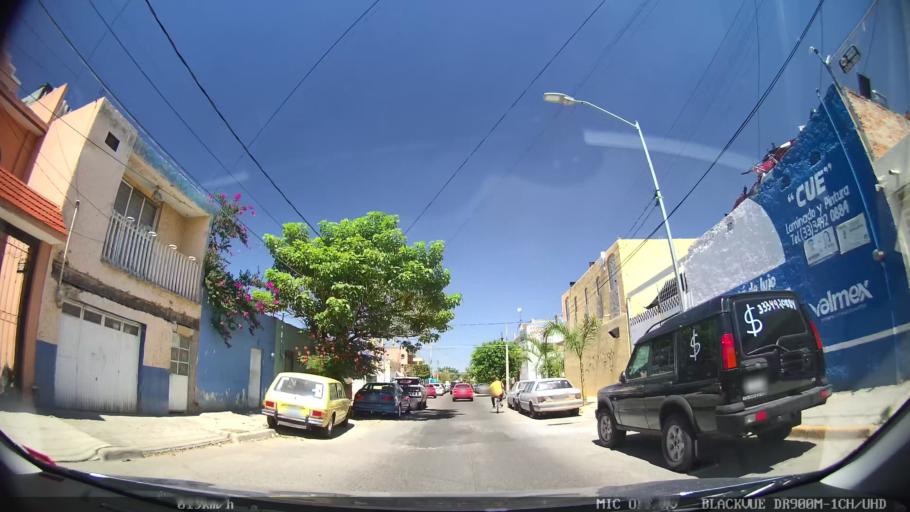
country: MX
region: Jalisco
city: Tlaquepaque
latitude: 20.6670
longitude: -103.2889
